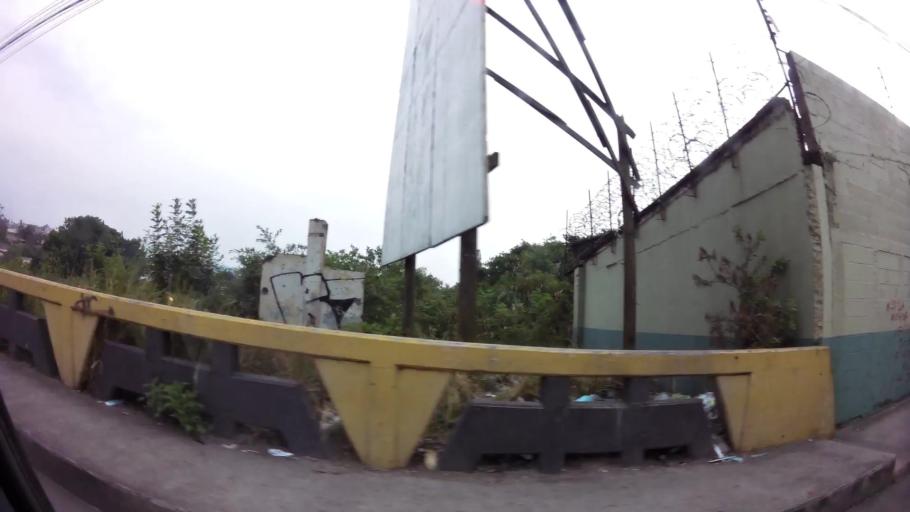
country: HN
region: Francisco Morazan
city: Tegucigalpa
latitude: 14.0894
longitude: -87.2053
